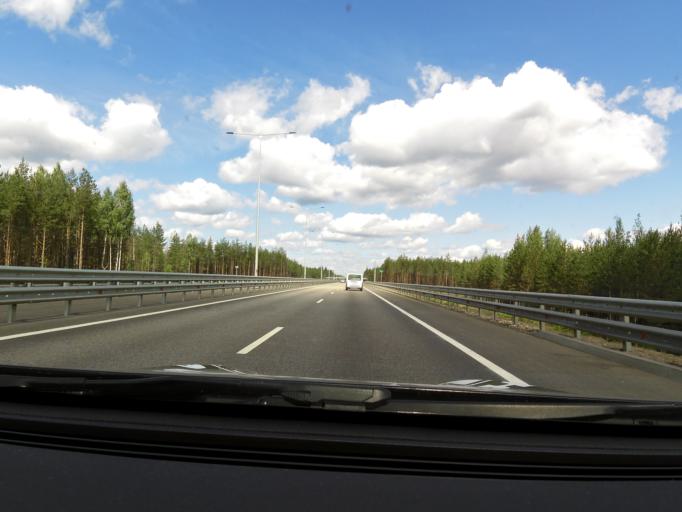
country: RU
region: Tverskaya
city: Krasnomayskiy
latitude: 57.5639
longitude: 34.2641
